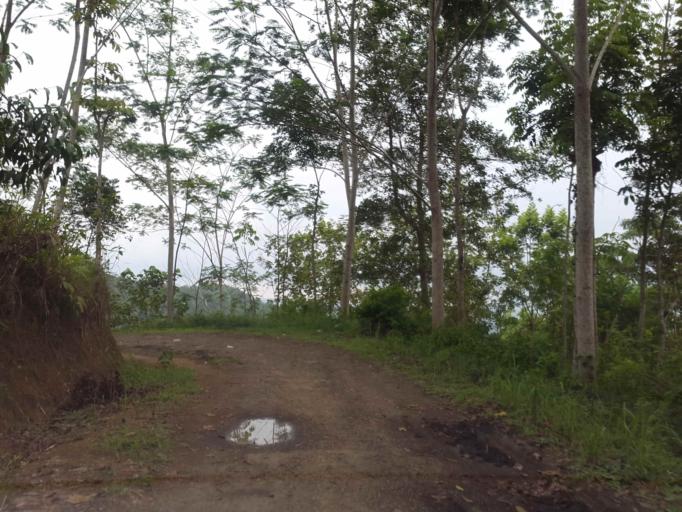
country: ID
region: Central Java
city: Jambuluwuk
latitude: -7.3318
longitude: 108.9372
